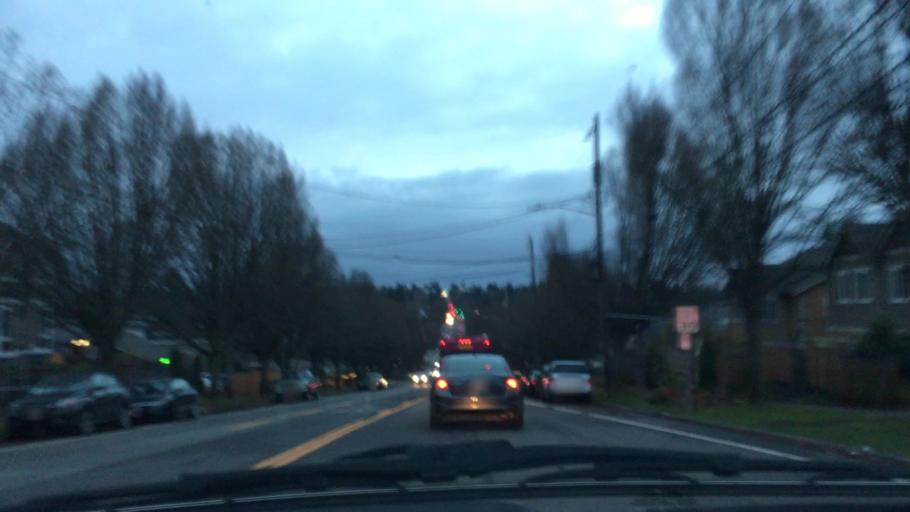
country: US
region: Washington
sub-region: King County
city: White Center
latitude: 47.5180
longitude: -122.3768
